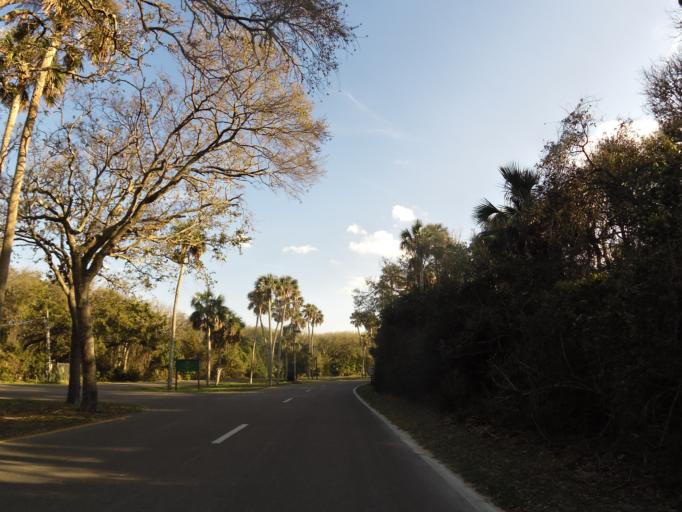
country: US
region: Florida
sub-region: Duval County
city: Atlantic Beach
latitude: 30.3660
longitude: -81.4005
